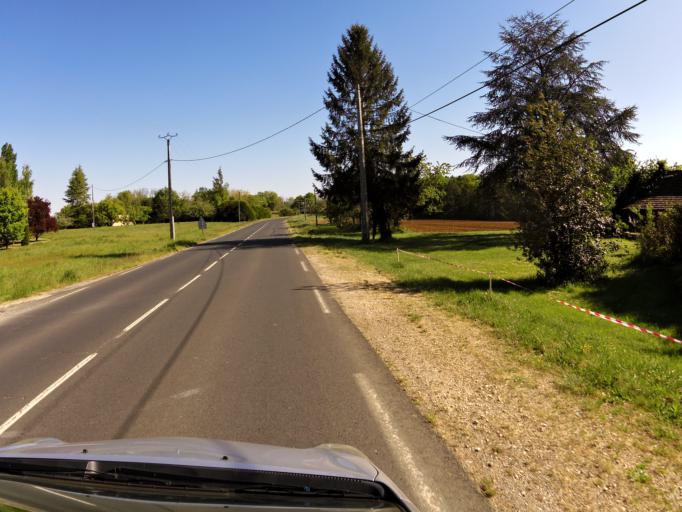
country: FR
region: Aquitaine
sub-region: Departement de la Dordogne
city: Montignac
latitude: 45.0068
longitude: 1.2416
